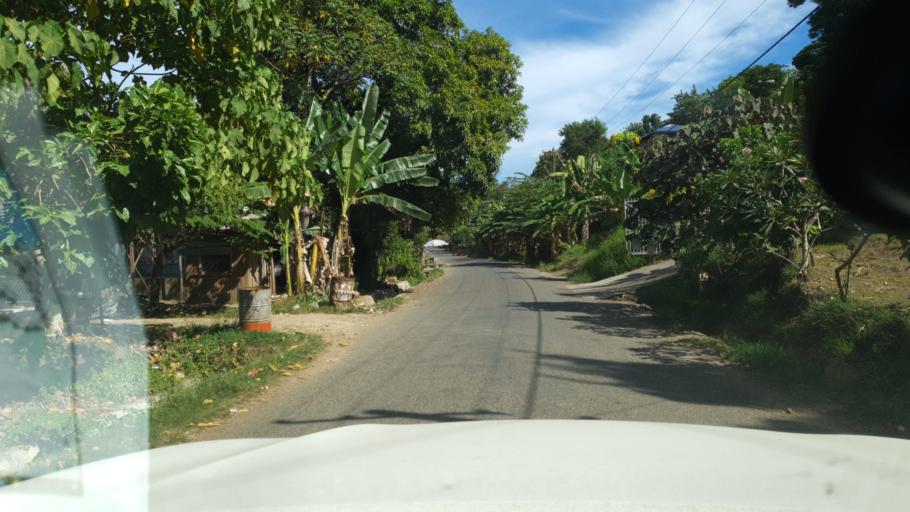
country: SB
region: Guadalcanal
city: Honiara
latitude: -9.4357
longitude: 159.9552
